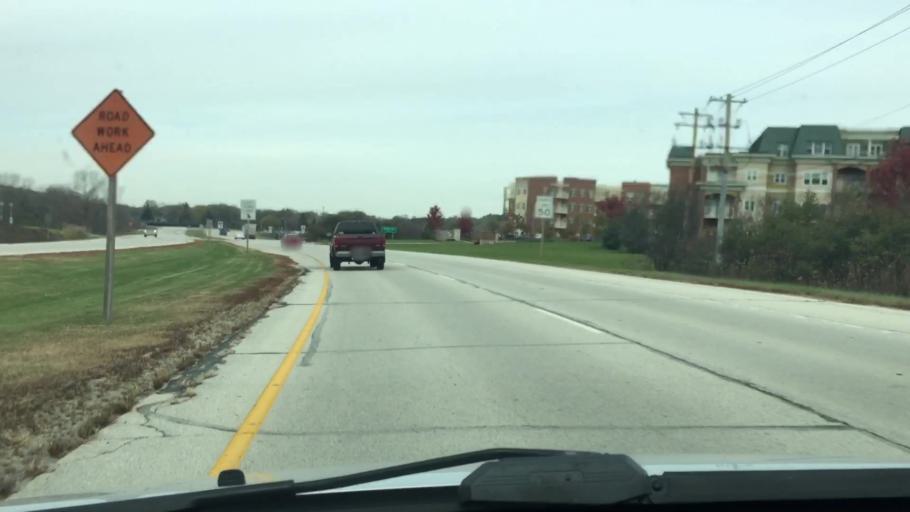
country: US
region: Wisconsin
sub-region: Milwaukee County
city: Franklin
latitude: 42.9105
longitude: -88.0402
